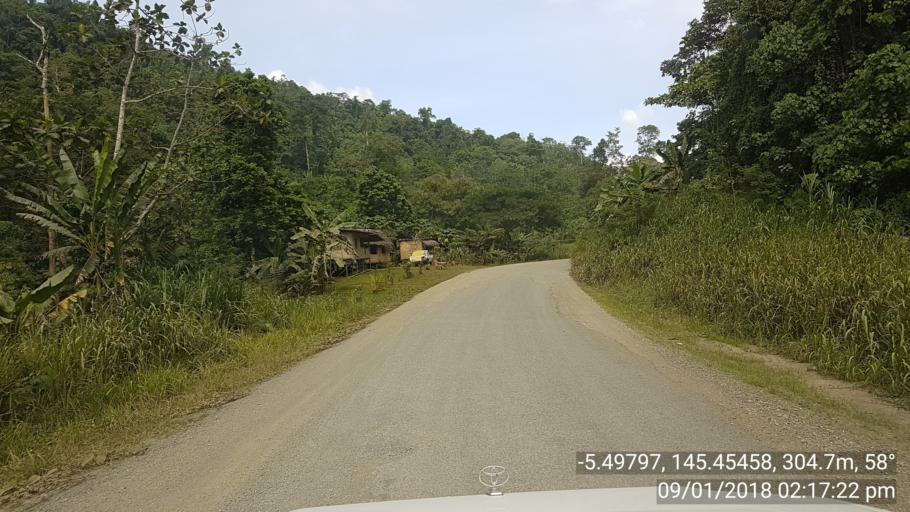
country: PG
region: Madang
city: Madang
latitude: -5.4981
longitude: 145.4546
